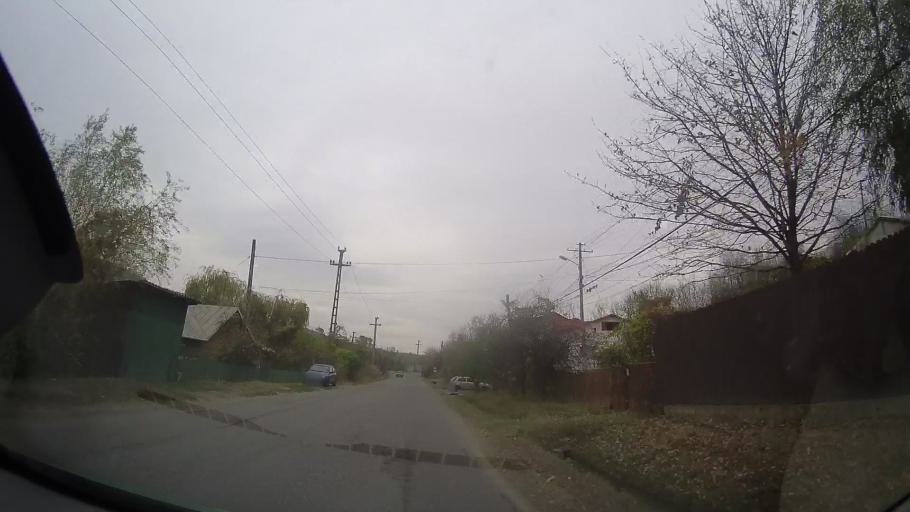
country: RO
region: Prahova
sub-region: Oras Urlati
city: Urlati
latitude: 45.0091
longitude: 26.2279
